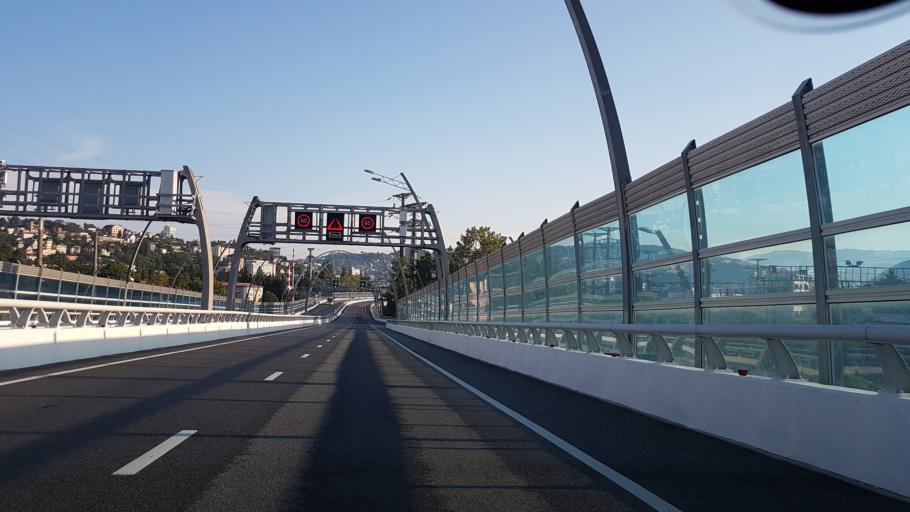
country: RU
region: Krasnodarskiy
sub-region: Sochi City
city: Sochi
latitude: 43.5978
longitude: 39.7311
